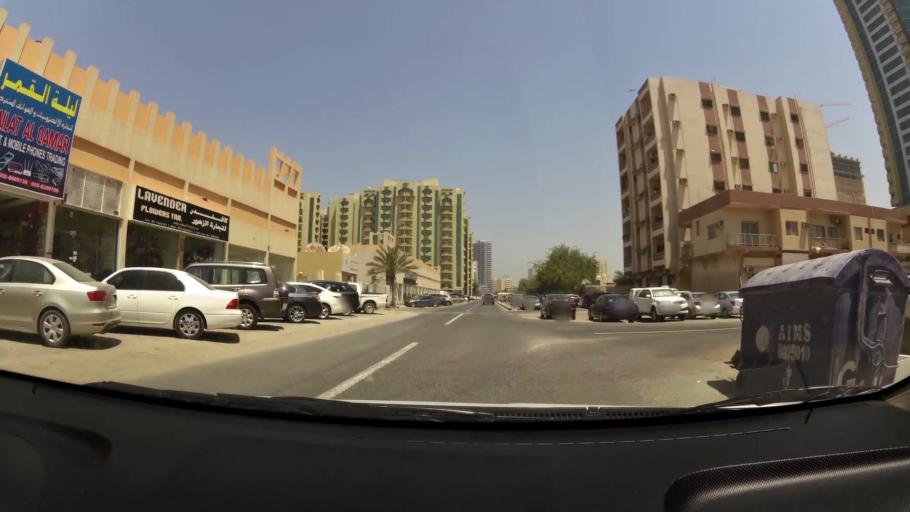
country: AE
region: Ajman
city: Ajman
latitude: 25.3936
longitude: 55.4534
